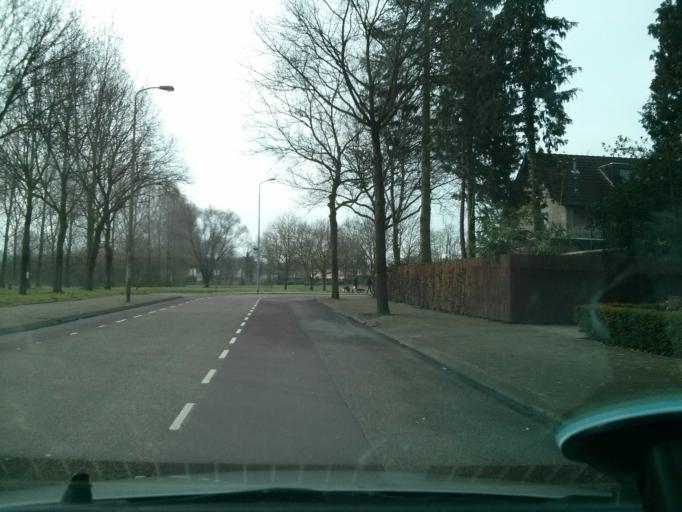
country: NL
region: North Brabant
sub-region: Gemeente Son en Breugel
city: Son
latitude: 51.4843
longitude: 5.5047
